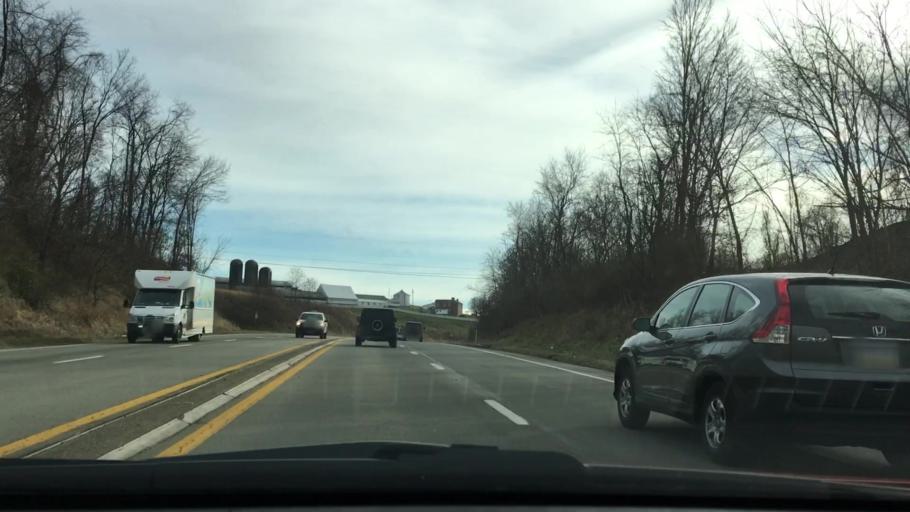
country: US
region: Pennsylvania
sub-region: Fayette County
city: Perryopolis
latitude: 40.0236
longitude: -79.7682
